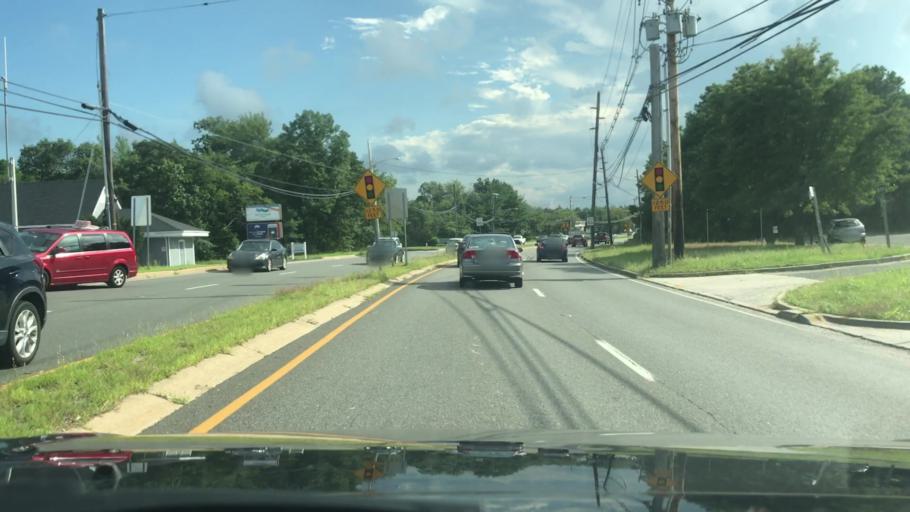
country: US
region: New Jersey
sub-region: Ocean County
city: Leisure Village East
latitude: 40.0077
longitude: -74.1482
